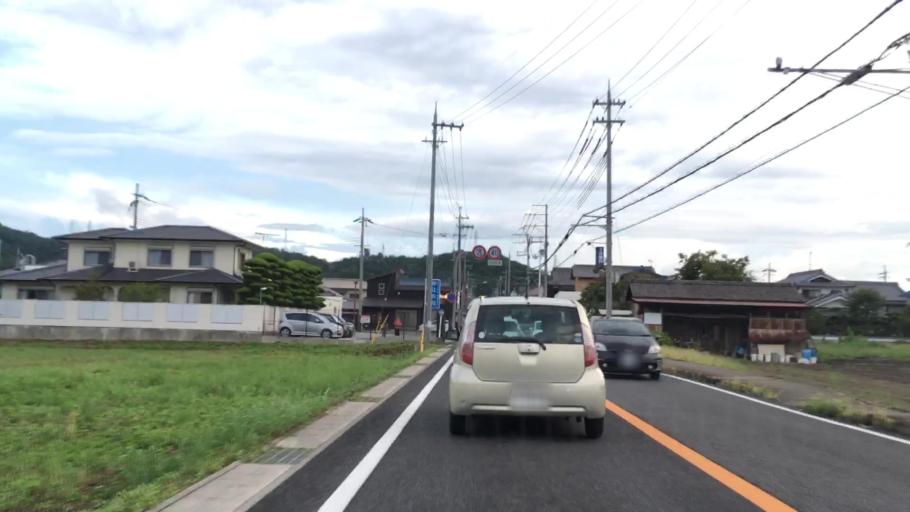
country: JP
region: Hyogo
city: Himeji
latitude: 34.8830
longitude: 134.7293
